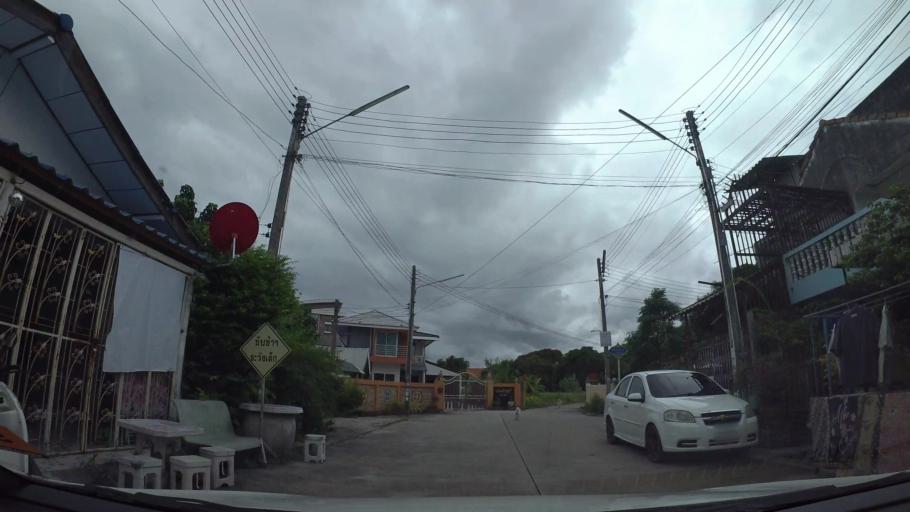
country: TH
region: Rayong
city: Rayong
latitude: 12.6731
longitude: 101.2737
